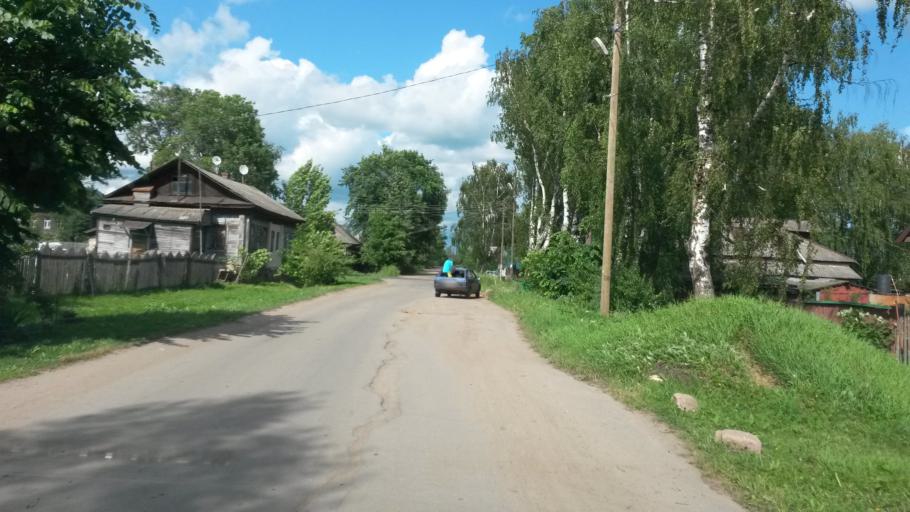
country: RU
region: Jaroslavl
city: Tutayev
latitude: 57.8878
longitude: 39.5367
